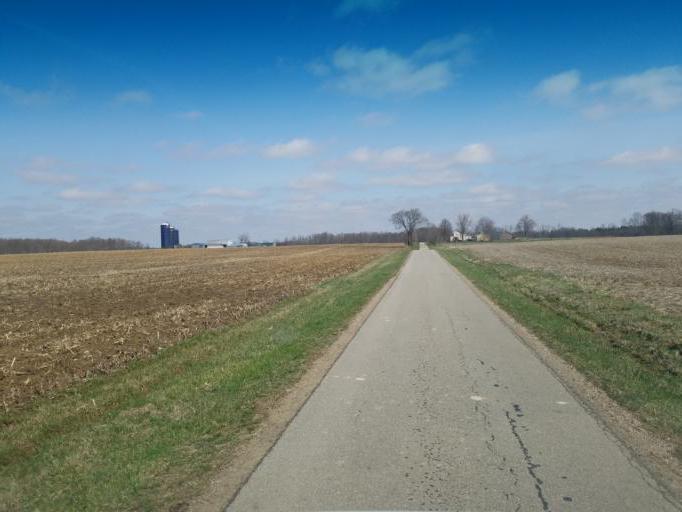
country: US
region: Ohio
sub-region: Crawford County
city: Bucyrus
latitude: 40.9233
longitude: -83.0598
